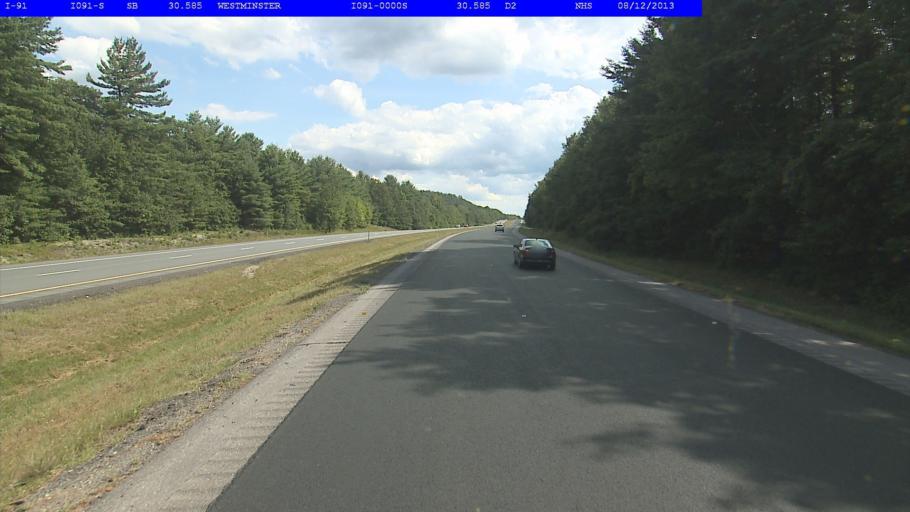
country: US
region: Vermont
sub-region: Windham County
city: Bellows Falls
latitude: 43.1184
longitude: -72.4621
